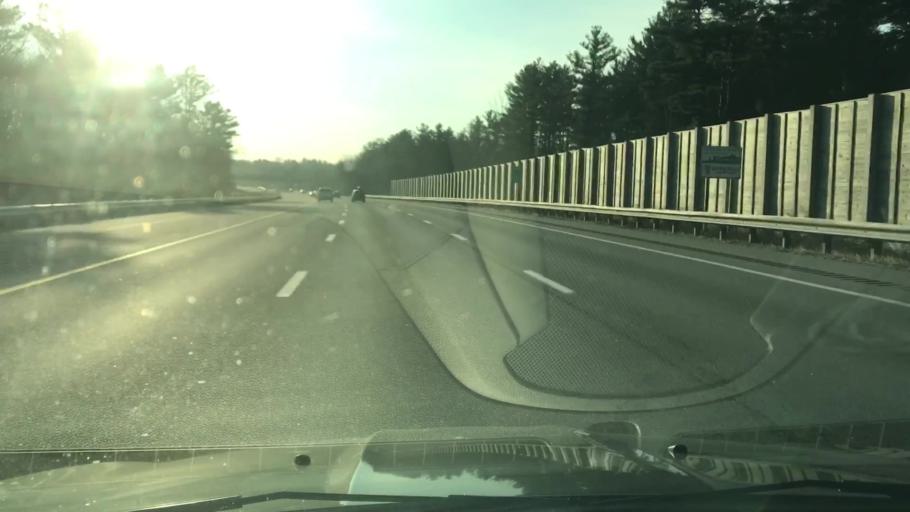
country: US
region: New Hampshire
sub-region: Rockingham County
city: Salem
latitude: 42.7644
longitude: -71.2374
